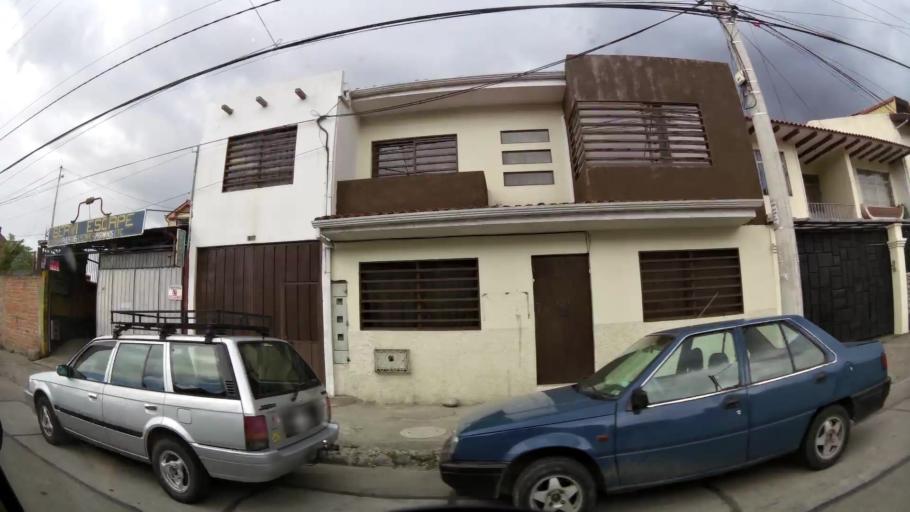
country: EC
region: Azuay
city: Cuenca
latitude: -2.8900
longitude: -79.0186
